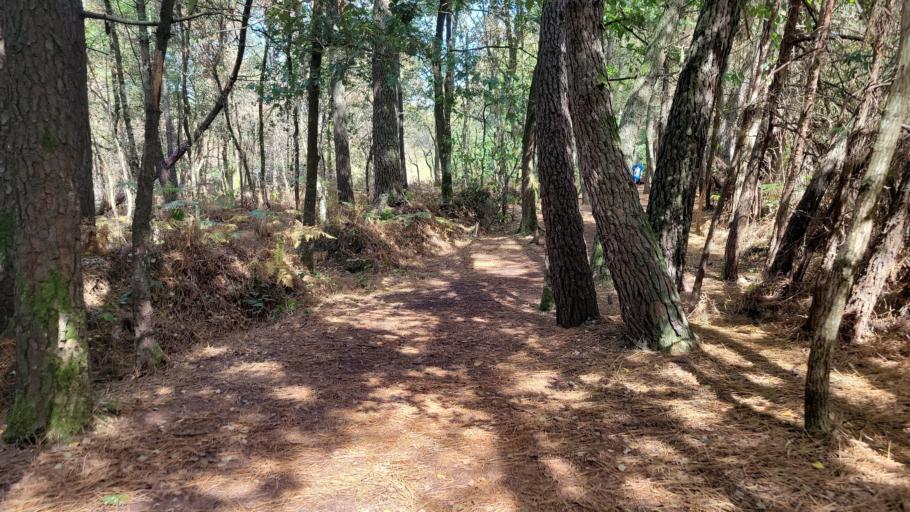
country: FR
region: Brittany
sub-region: Departement du Morbihan
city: Mauron
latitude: 48.0408
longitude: -2.2513
